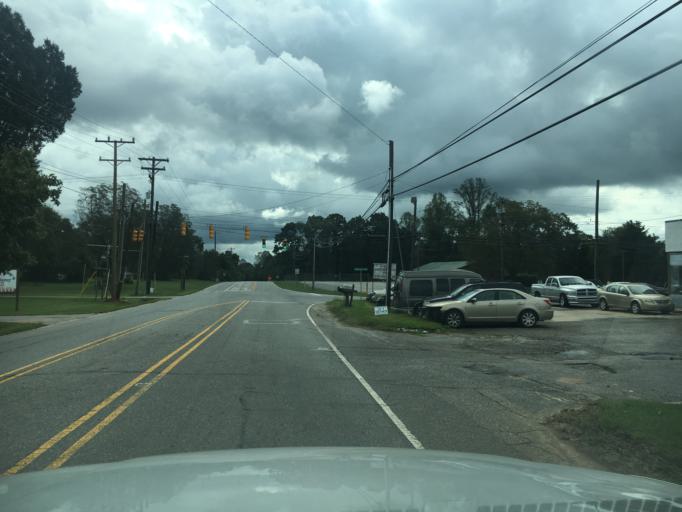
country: US
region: North Carolina
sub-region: Catawba County
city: Saint Stephens
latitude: 35.7229
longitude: -81.2646
